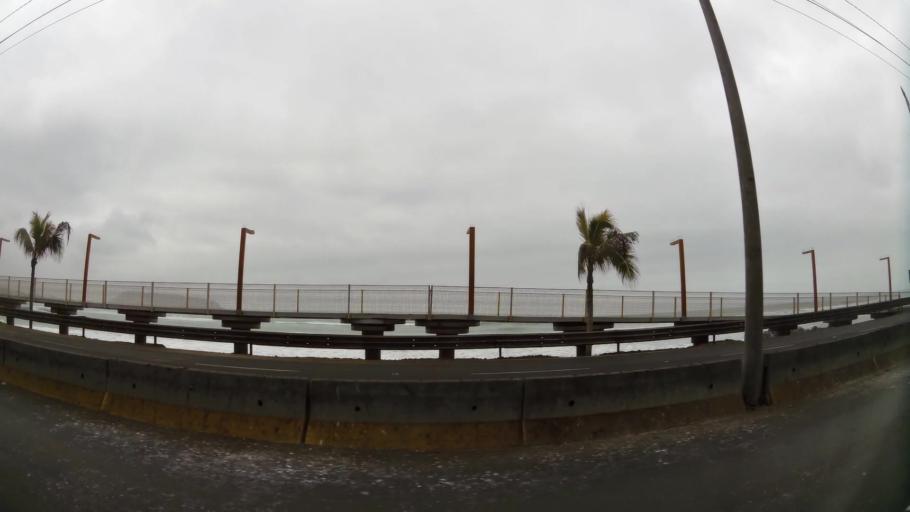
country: PE
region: Lima
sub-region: Lima
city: San Isidro
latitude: -12.1239
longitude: -77.0414
